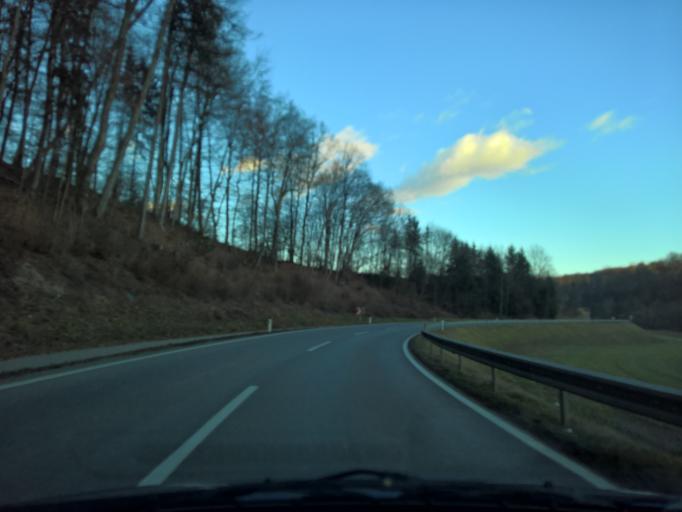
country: AT
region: Styria
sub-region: Politischer Bezirk Leibnitz
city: Ehrenhausen
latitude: 46.7195
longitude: 15.5791
